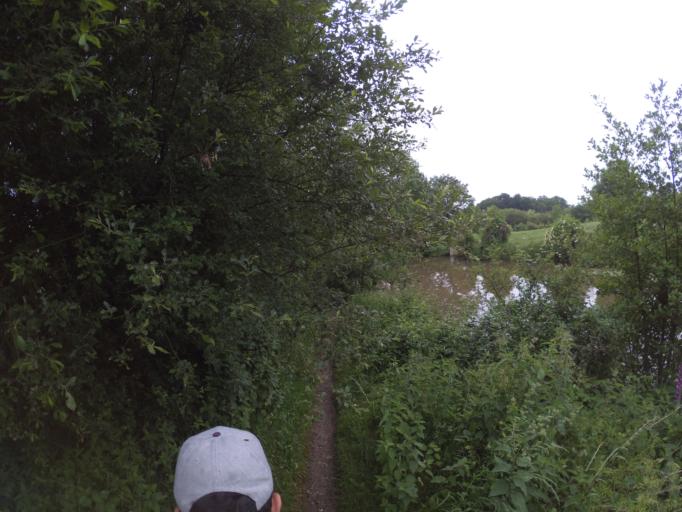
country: FR
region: Pays de la Loire
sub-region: Departement de la Vendee
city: Nesmy
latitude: 46.6168
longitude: -1.4052
